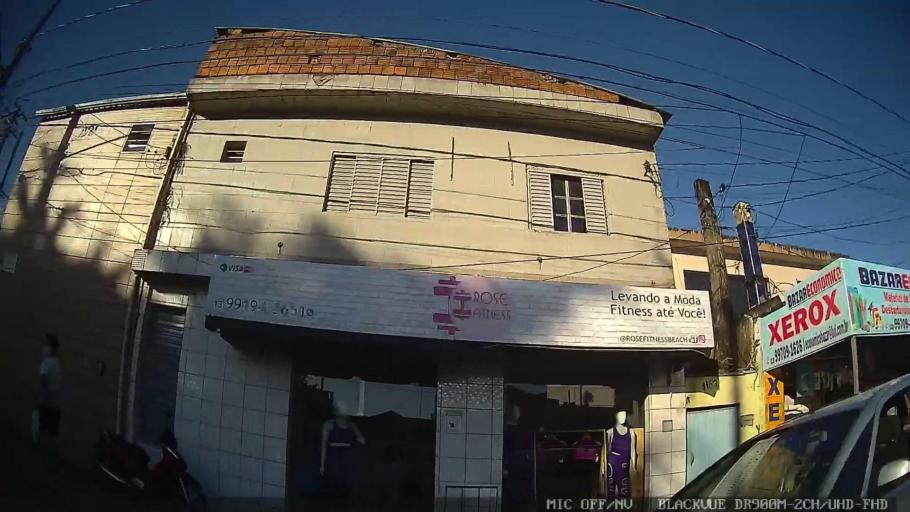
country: BR
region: Sao Paulo
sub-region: Santos
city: Santos
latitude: -23.9491
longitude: -46.2922
